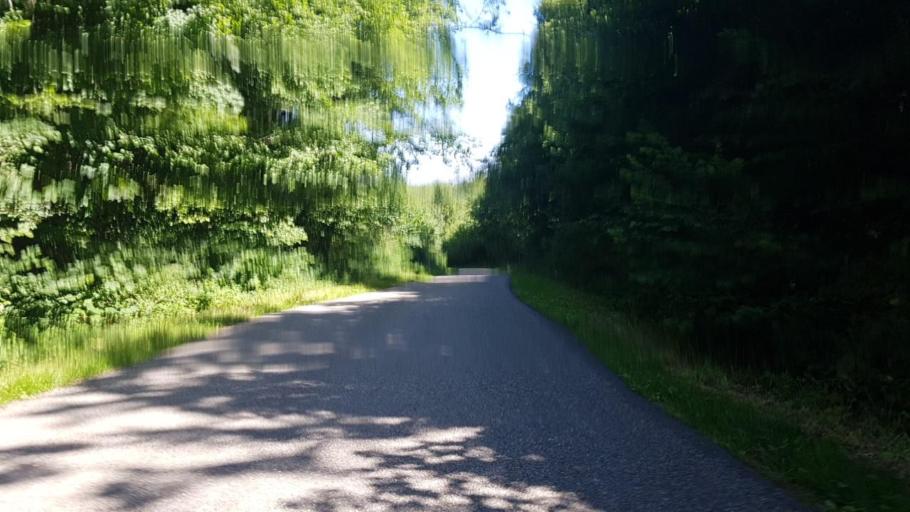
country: BE
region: Wallonia
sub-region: Province du Hainaut
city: Momignies
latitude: 50.0815
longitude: 4.2281
